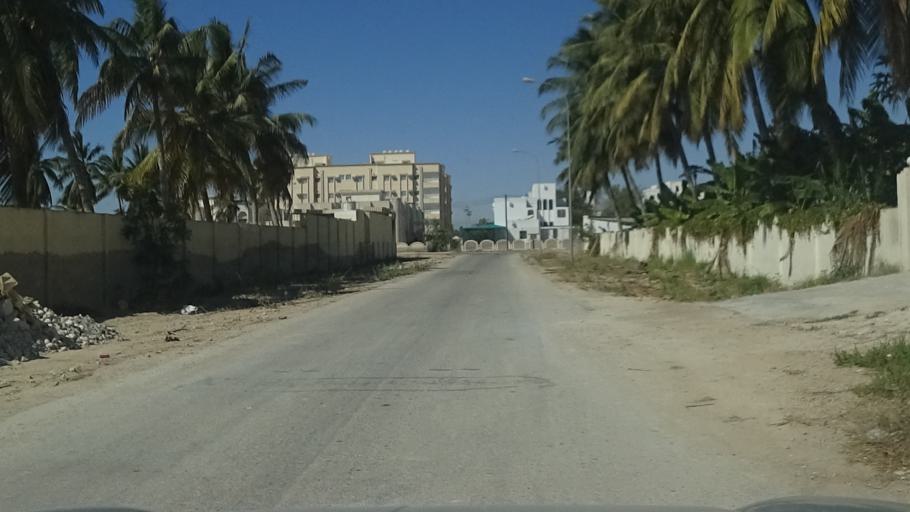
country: OM
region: Zufar
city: Salalah
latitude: 17.0288
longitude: 54.1614
